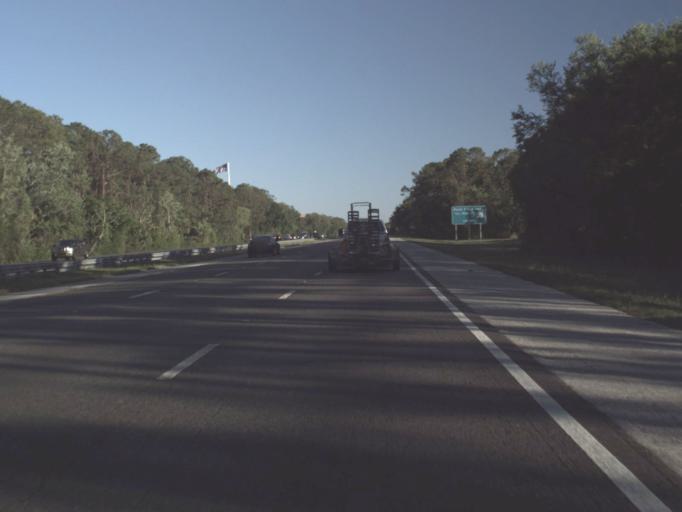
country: US
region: Florida
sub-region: Flagler County
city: Palm Coast
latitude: 29.5696
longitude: -81.2292
